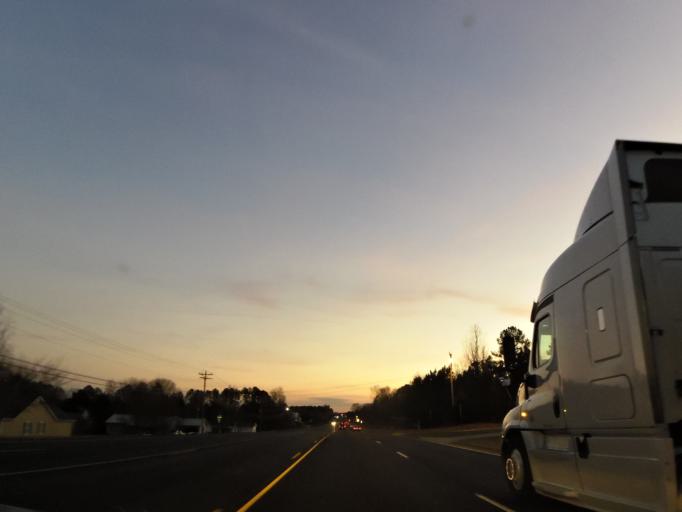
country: US
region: Georgia
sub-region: Whitfield County
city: Varnell
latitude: 34.9114
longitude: -84.9461
